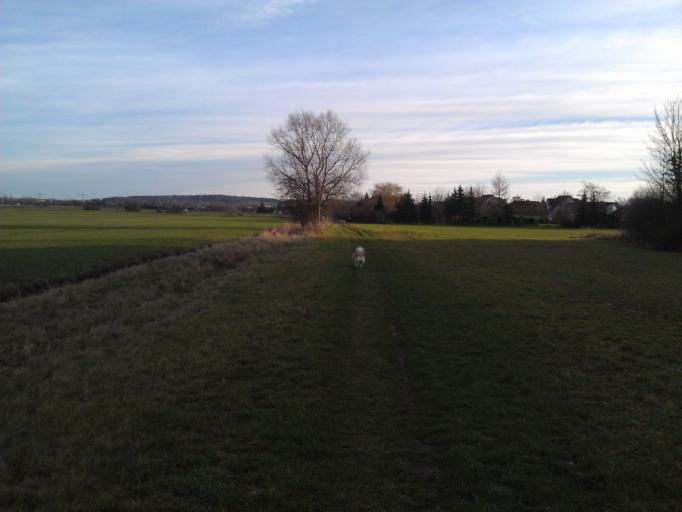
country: DE
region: Thuringia
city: Emleben
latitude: 50.9220
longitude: 10.6774
